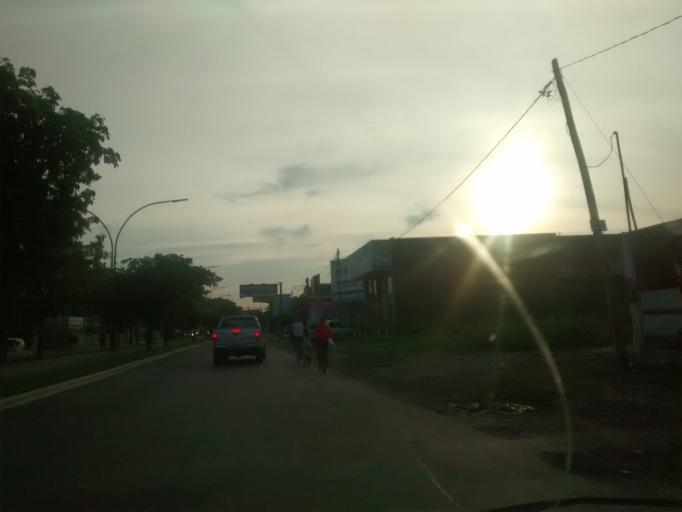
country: AR
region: Chaco
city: Resistencia
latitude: -27.4351
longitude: -58.9687
